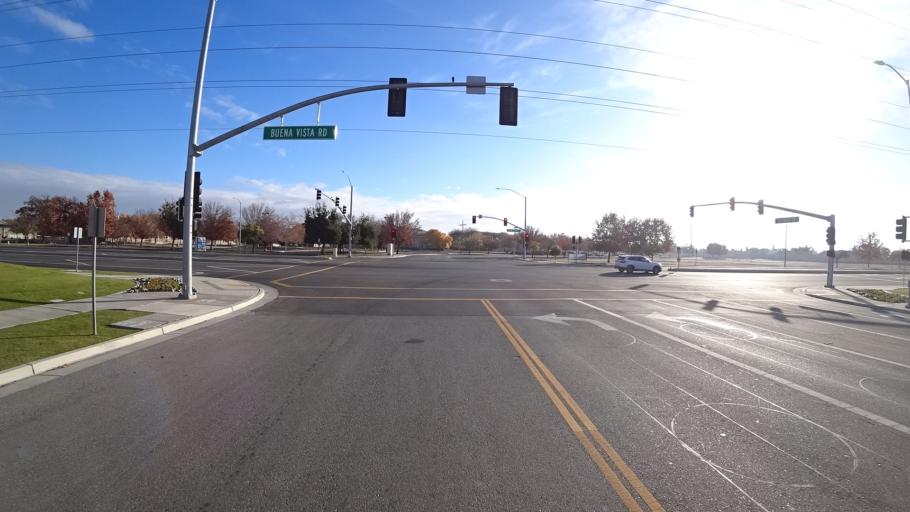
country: US
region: California
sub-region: Kern County
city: Rosedale
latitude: 35.3125
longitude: -119.1285
